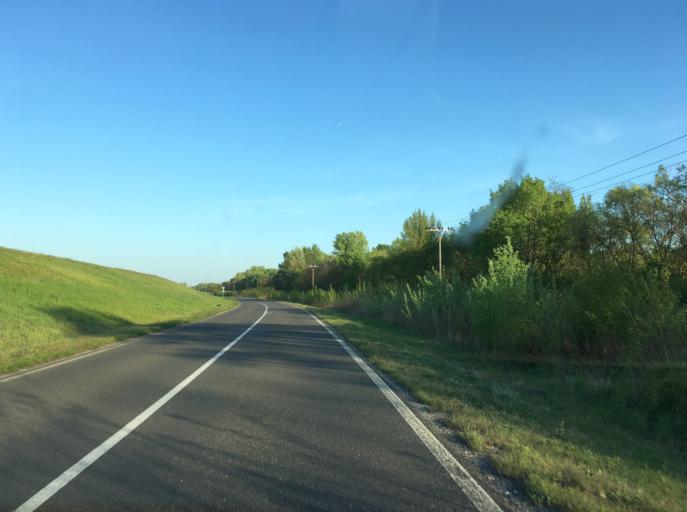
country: HU
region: Gyor-Moson-Sopron
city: Rajka
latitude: 48.0031
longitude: 17.2560
